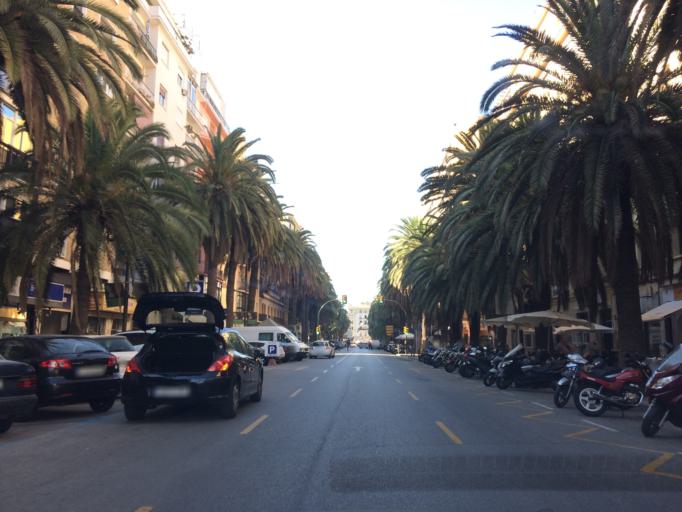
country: ES
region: Andalusia
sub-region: Provincia de Malaga
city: Malaga
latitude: 36.7142
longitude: -4.4243
